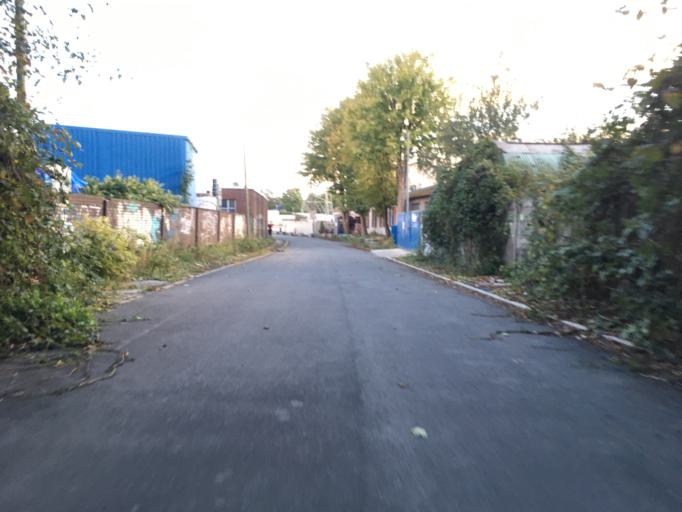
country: DE
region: North Rhine-Westphalia
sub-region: Regierungsbezirk Munster
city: Bottrop
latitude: 51.4900
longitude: 6.9227
